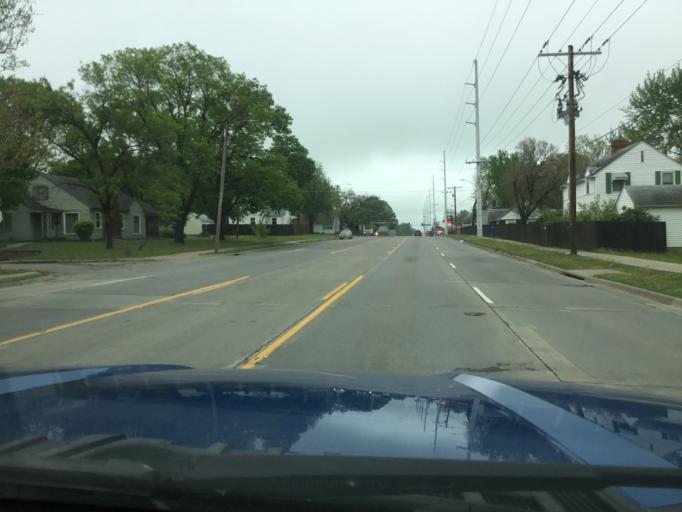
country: US
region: Kansas
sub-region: Shawnee County
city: Topeka
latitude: 39.0296
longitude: -95.7136
